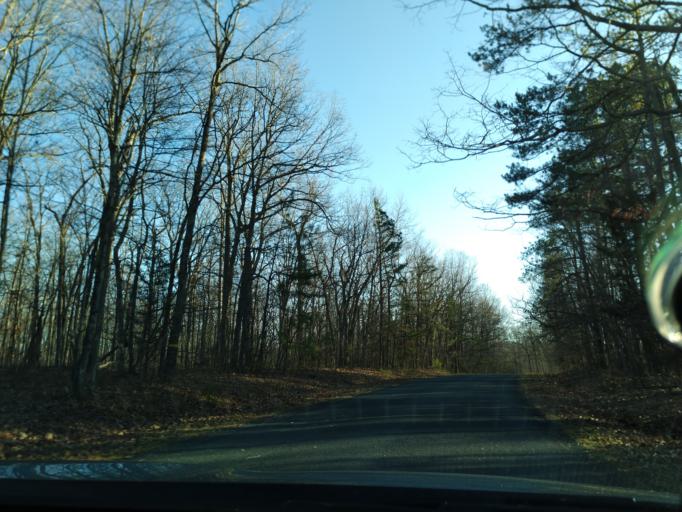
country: US
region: Virginia
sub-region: Appomattox County
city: Appomattox
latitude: 37.3951
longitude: -78.6582
